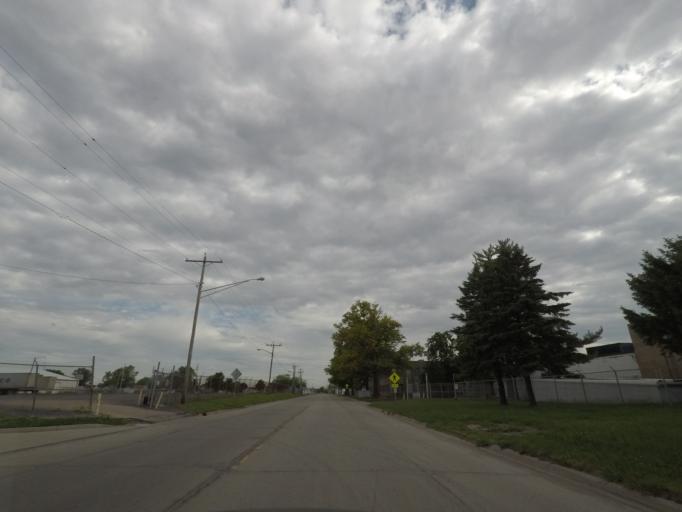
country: US
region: Illinois
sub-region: Logan County
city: Lincoln
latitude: 40.1408
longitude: -89.3488
